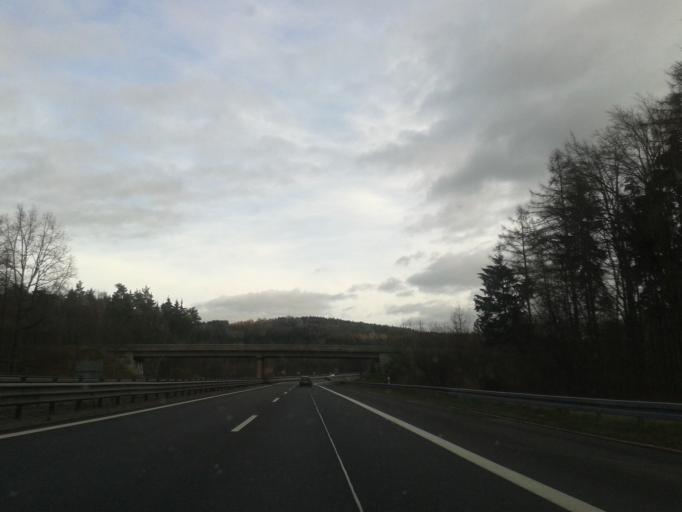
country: DE
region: Saxony
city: Hauswalde
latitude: 51.1742
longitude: 14.0918
